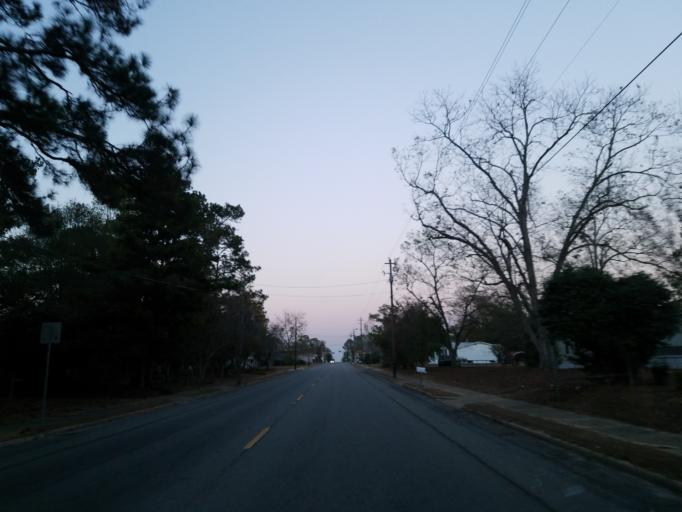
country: US
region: Georgia
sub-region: Wilcox County
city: Rochelle
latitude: 31.8044
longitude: -83.4889
